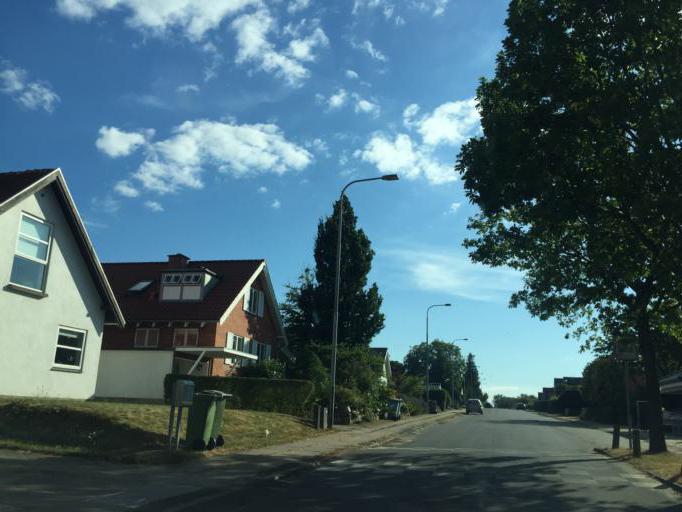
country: DK
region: South Denmark
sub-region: Odense Kommune
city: Odense
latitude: 55.3730
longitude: 10.3599
